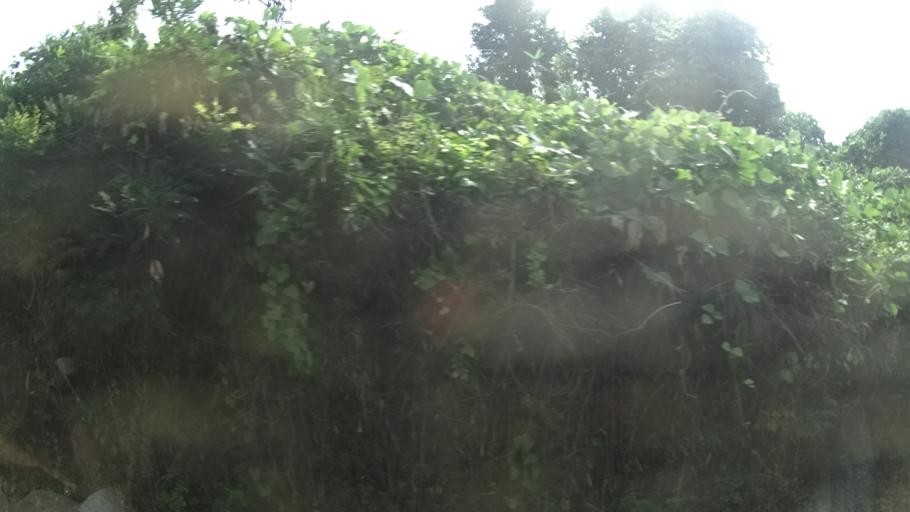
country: JP
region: Tochigi
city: Kanuma
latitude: 36.6348
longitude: 139.7290
